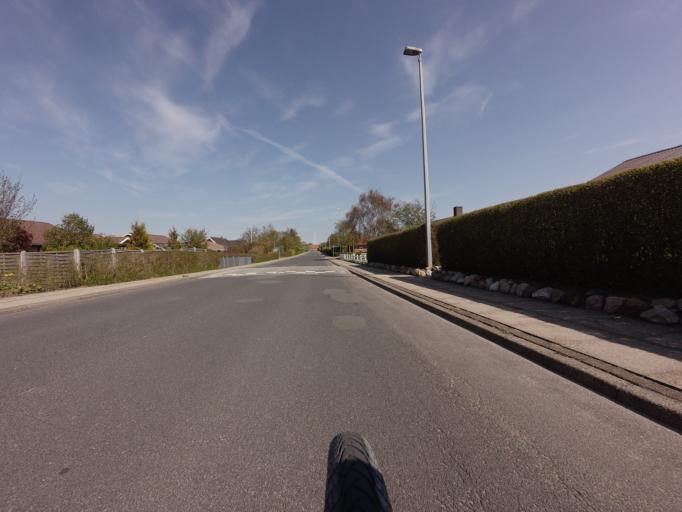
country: DK
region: North Denmark
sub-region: Jammerbugt Kommune
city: Pandrup
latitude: 57.2217
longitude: 9.6701
